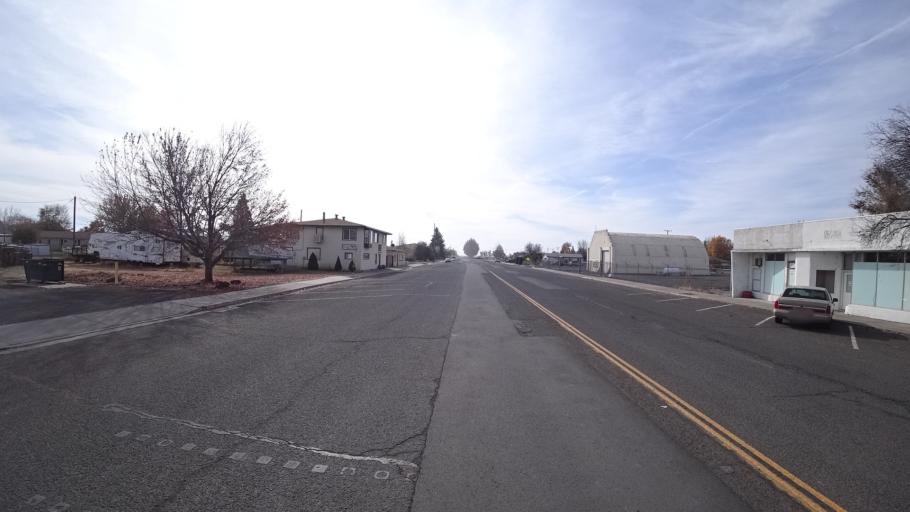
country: US
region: California
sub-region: Siskiyou County
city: Tulelake
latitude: 41.9533
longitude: -121.4767
